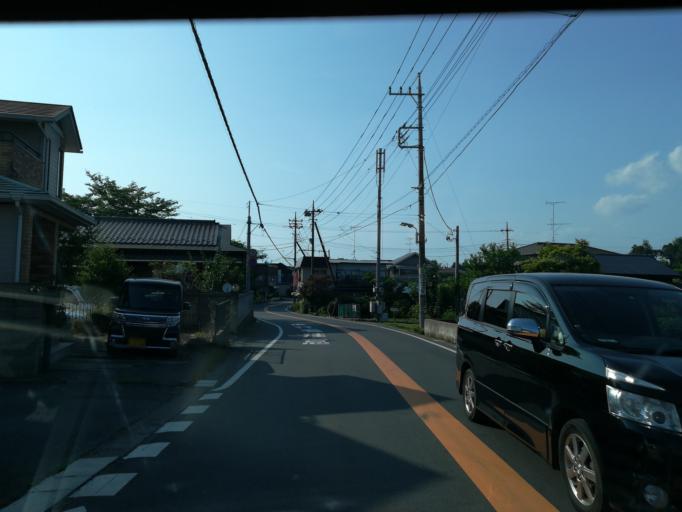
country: JP
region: Saitama
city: Sayama
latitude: 35.7921
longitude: 139.4084
